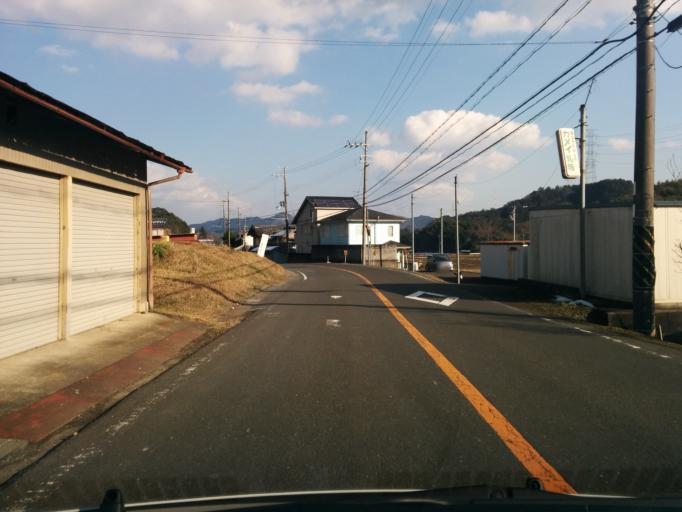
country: JP
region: Kyoto
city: Ayabe
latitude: 35.3645
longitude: 135.2022
